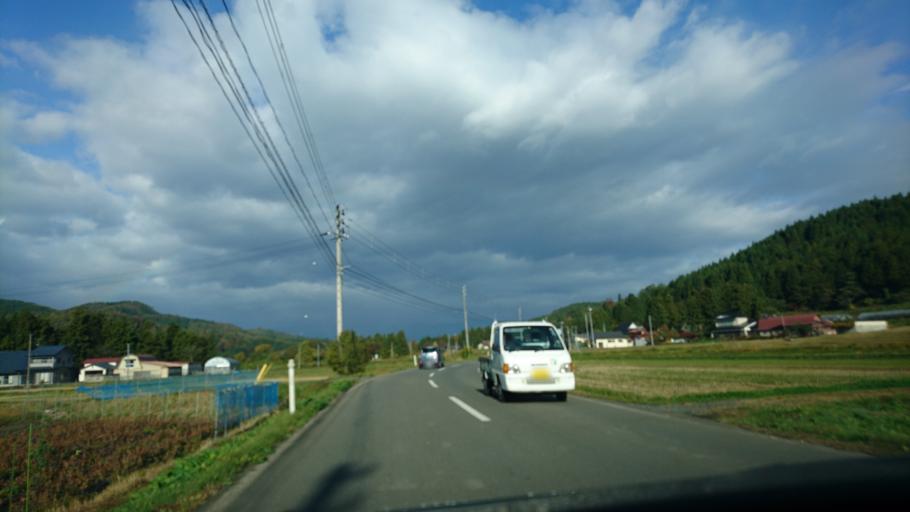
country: JP
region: Iwate
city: Mizusawa
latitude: 39.0570
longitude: 141.0387
